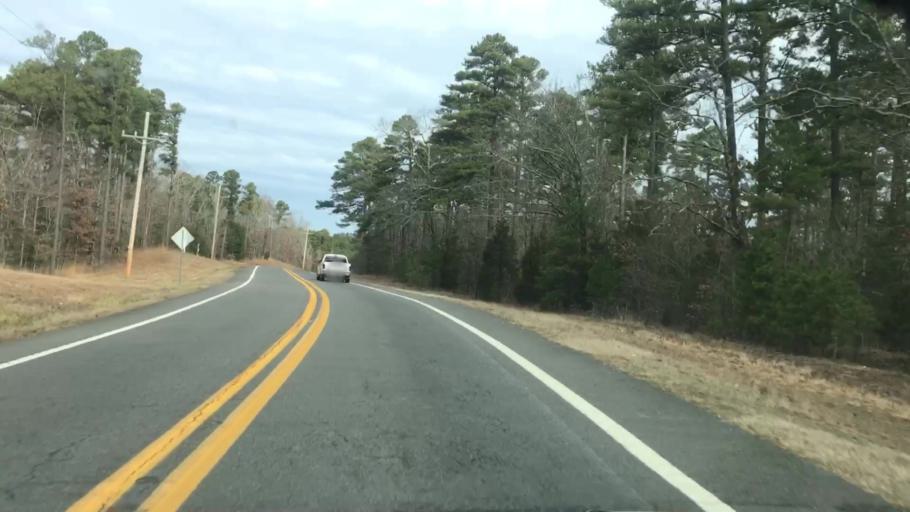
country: US
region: Arkansas
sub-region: Montgomery County
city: Mount Ida
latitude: 34.5880
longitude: -93.6635
